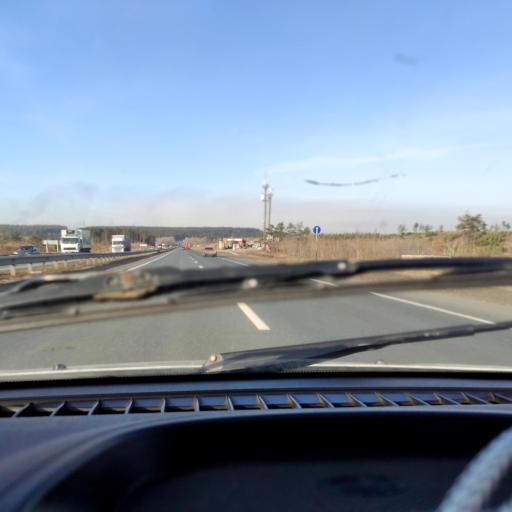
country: RU
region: Samara
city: Zhigulevsk
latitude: 53.5201
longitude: 49.5326
